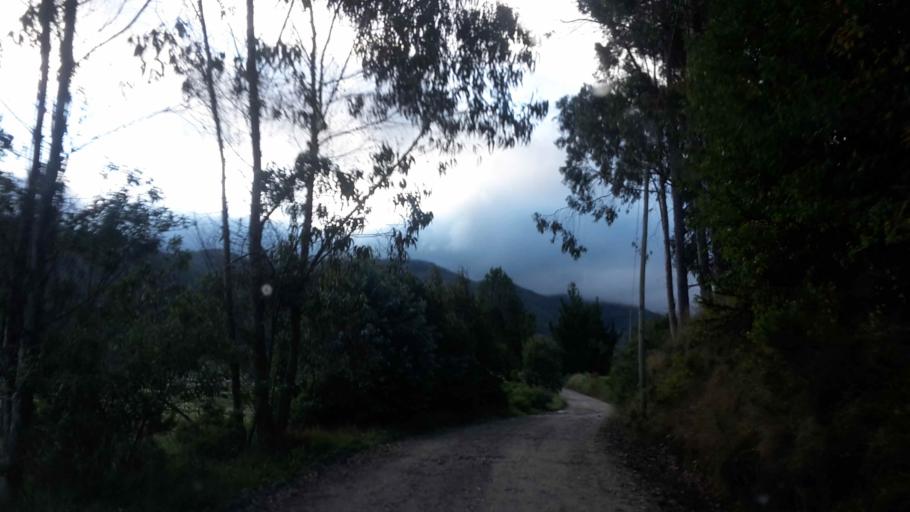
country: BO
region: Cochabamba
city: Colomi
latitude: -17.2778
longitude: -65.9134
